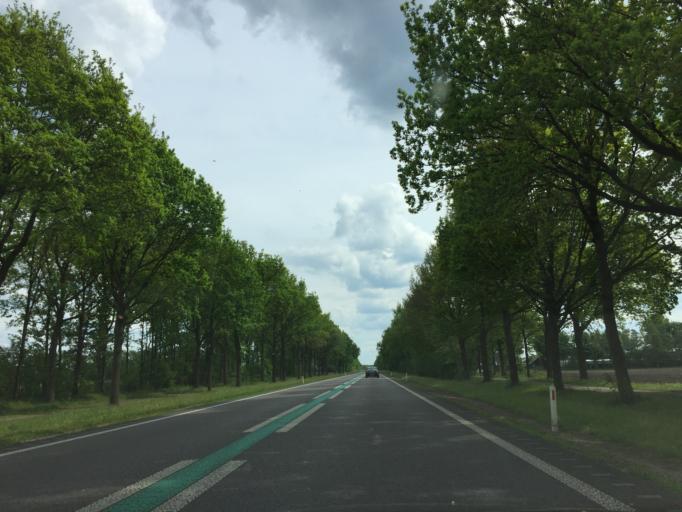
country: NL
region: Drenthe
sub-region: Gemeente Borger-Odoorn
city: Borger
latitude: 52.9892
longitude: 6.7636
